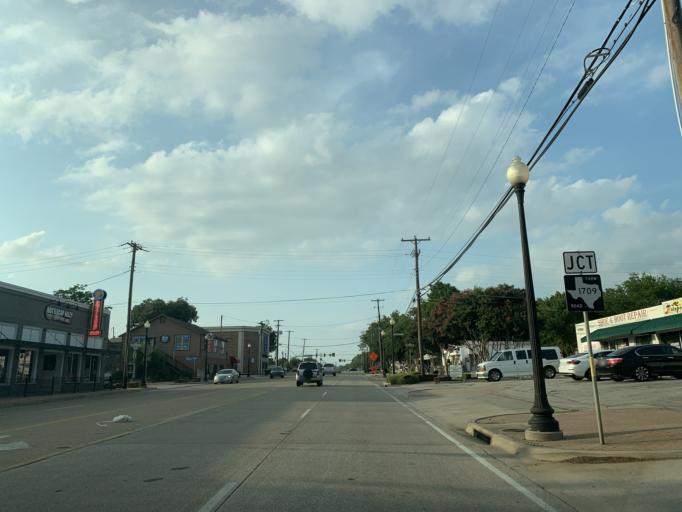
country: US
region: Texas
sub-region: Tarrant County
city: Keller
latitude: 32.9325
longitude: -97.2537
